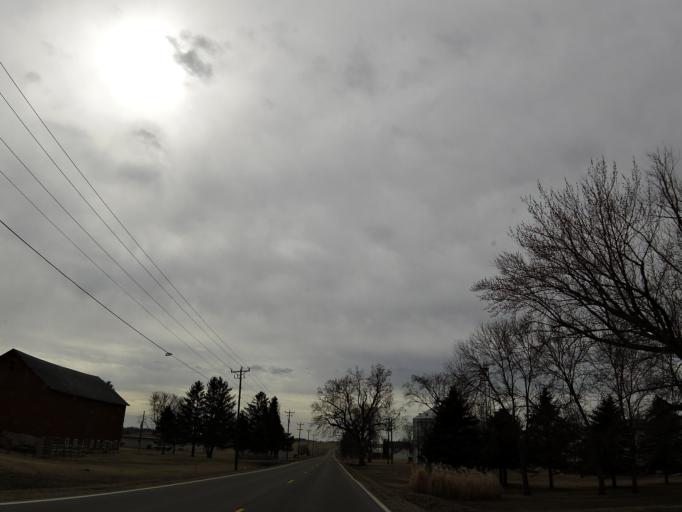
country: US
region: Minnesota
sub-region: Washington County
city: Afton
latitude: 44.8703
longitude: -92.8426
